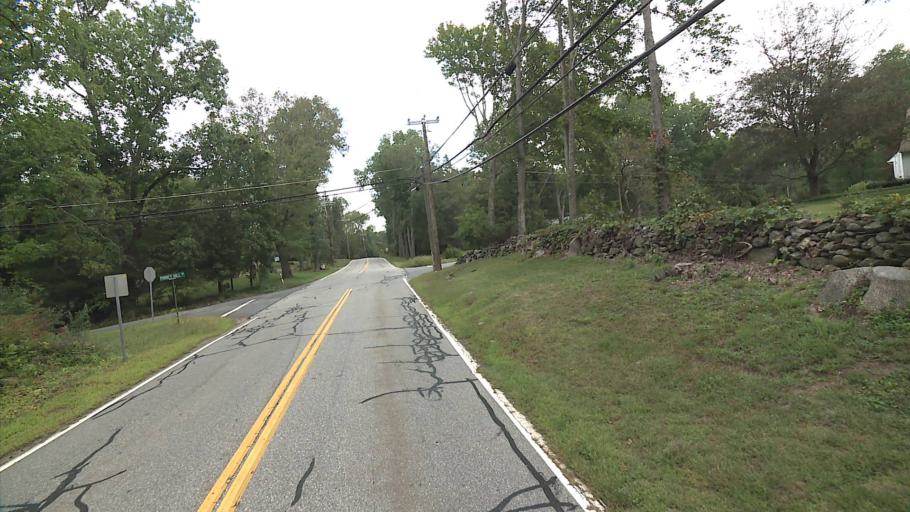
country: US
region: Connecticut
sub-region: Tolland County
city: Storrs
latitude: 41.8503
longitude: -72.2731
